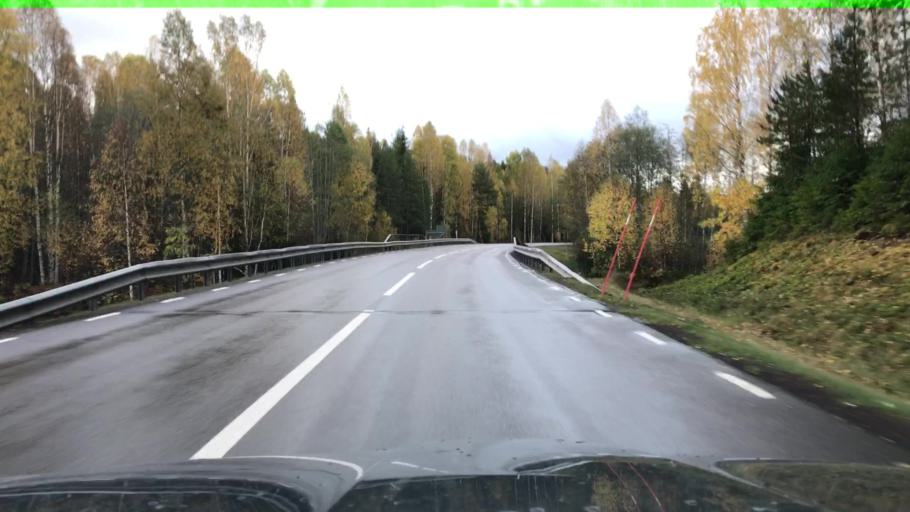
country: SE
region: Vaermland
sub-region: Hagfors Kommun
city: Ekshaerad
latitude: 60.4294
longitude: 13.2453
